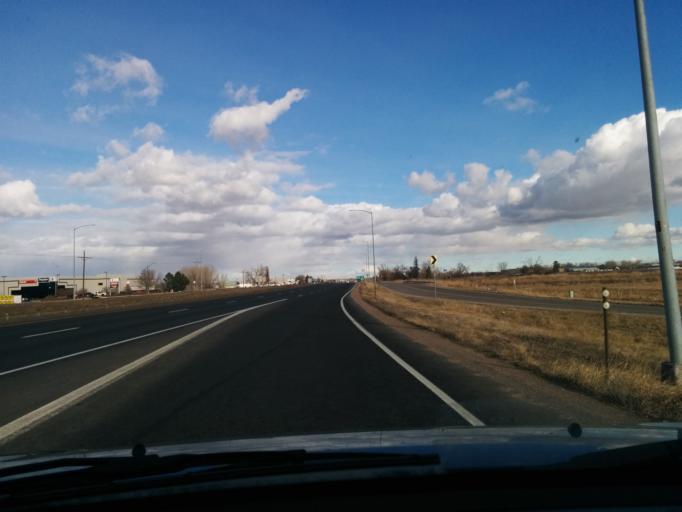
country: US
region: Colorado
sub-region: Larimer County
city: Fort Collins
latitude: 40.5689
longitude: -105.0011
